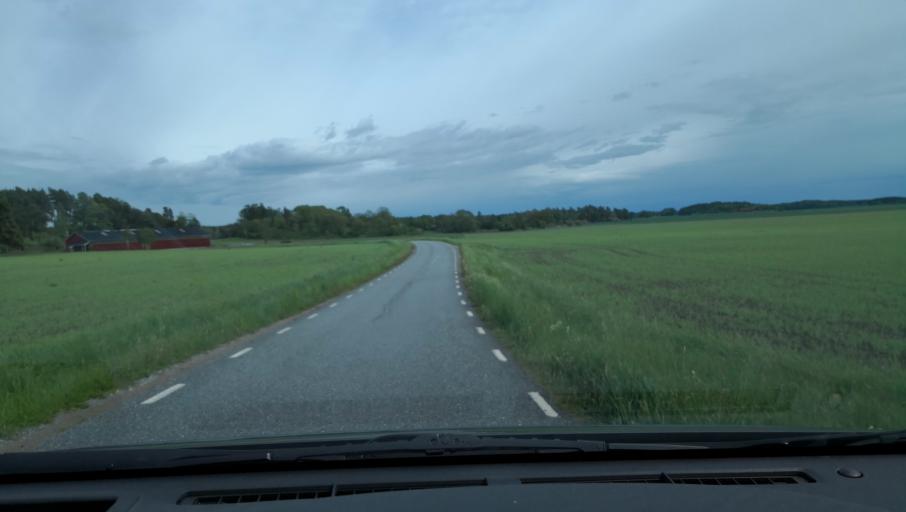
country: SE
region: Uppsala
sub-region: Enkopings Kommun
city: Orsundsbro
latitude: 59.7055
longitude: 17.4016
